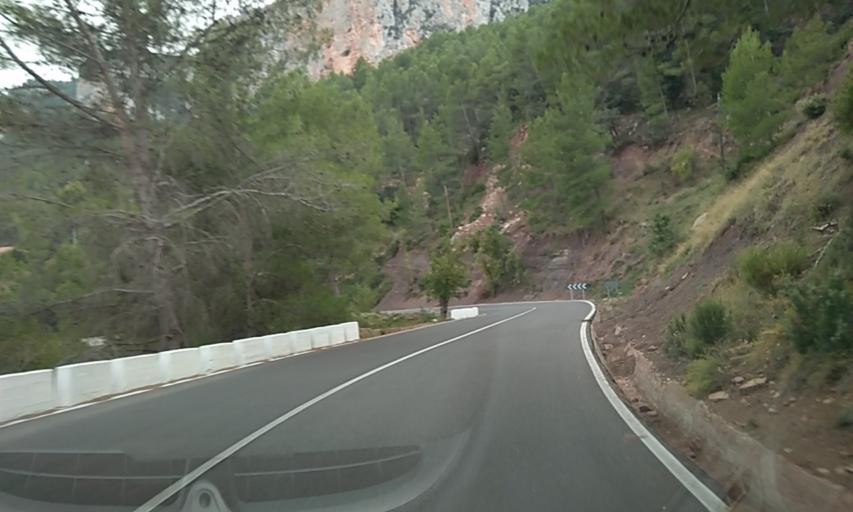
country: ES
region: Valencia
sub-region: Provincia de Castello
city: Puebla de Arenoso
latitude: 40.0859
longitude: -0.5550
